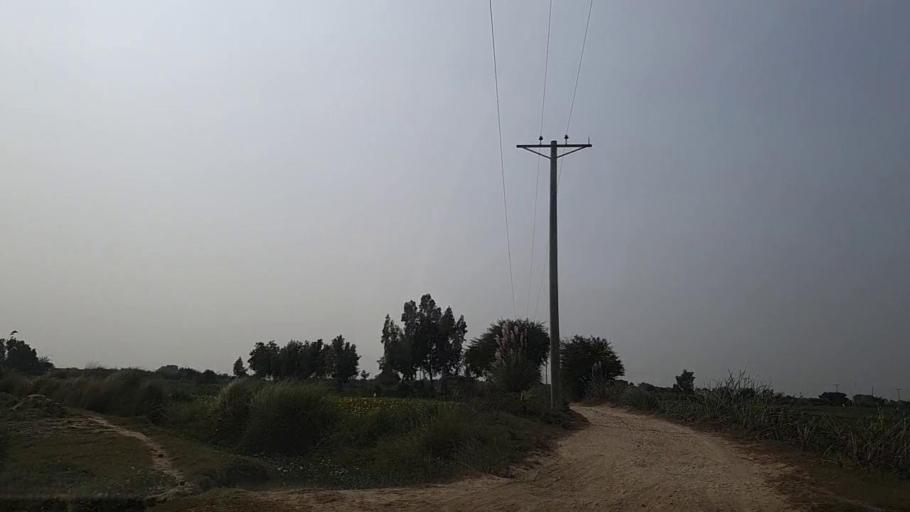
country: PK
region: Sindh
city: Mirpur Sakro
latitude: 24.6177
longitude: 67.7415
